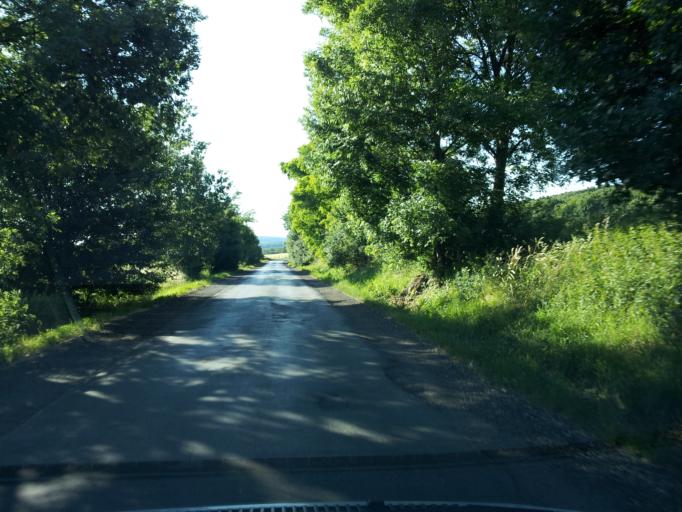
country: HU
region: Veszprem
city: Zirc
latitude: 47.2111
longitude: 17.8445
